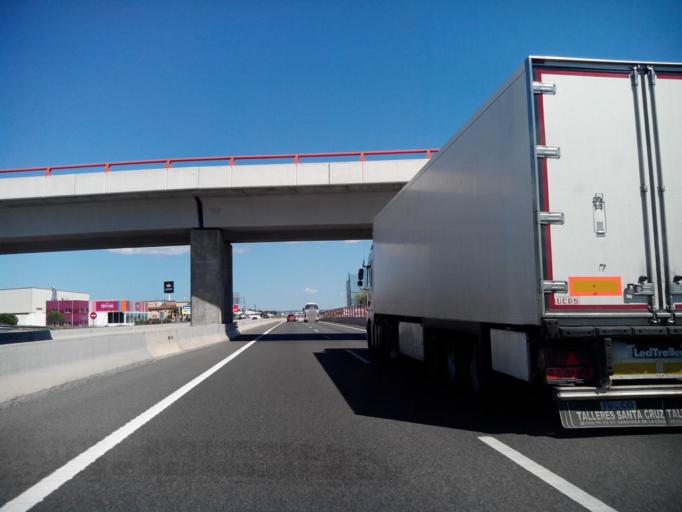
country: ES
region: Catalonia
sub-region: Provincia de Tarragona
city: Cambrils
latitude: 41.0885
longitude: 1.0901
